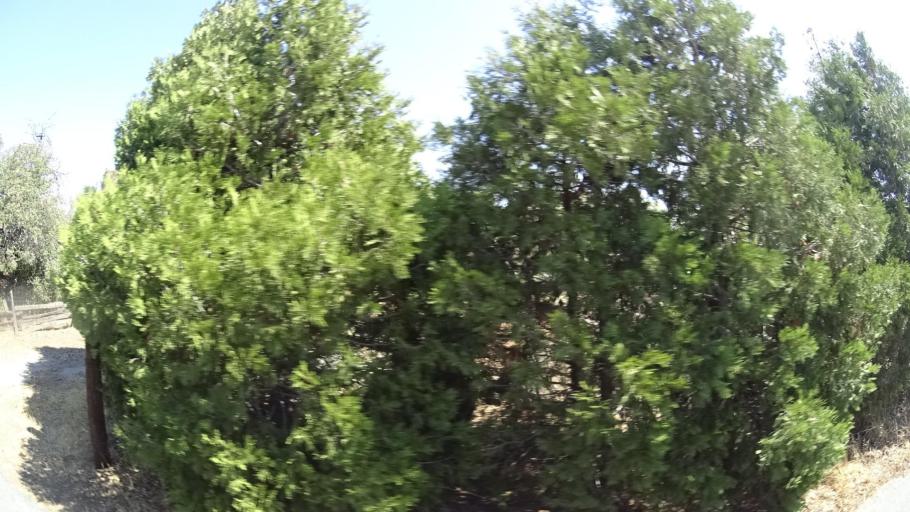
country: US
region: California
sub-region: San Diego County
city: Julian
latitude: 33.0757
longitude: -116.5883
